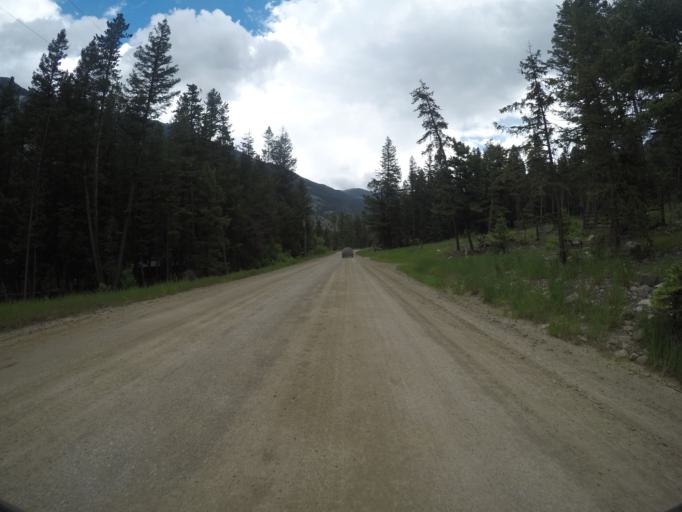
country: US
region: Montana
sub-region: Park County
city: Livingston
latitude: 45.4905
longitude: -110.2212
